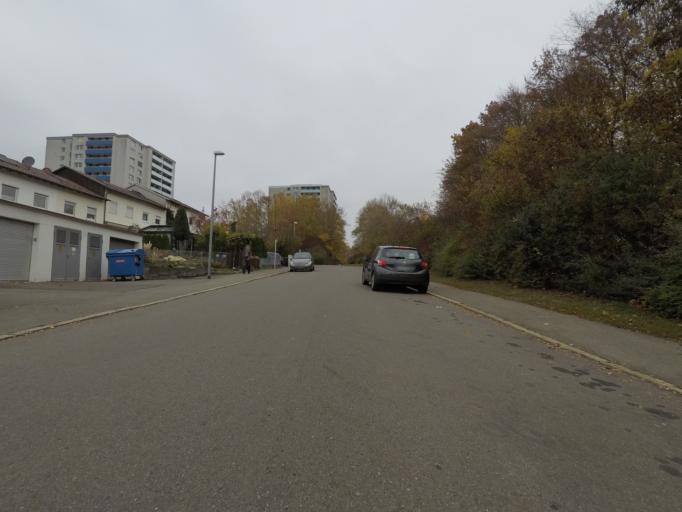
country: DE
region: Baden-Wuerttemberg
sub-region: Tuebingen Region
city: Reutlingen
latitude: 48.5127
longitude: 9.2105
